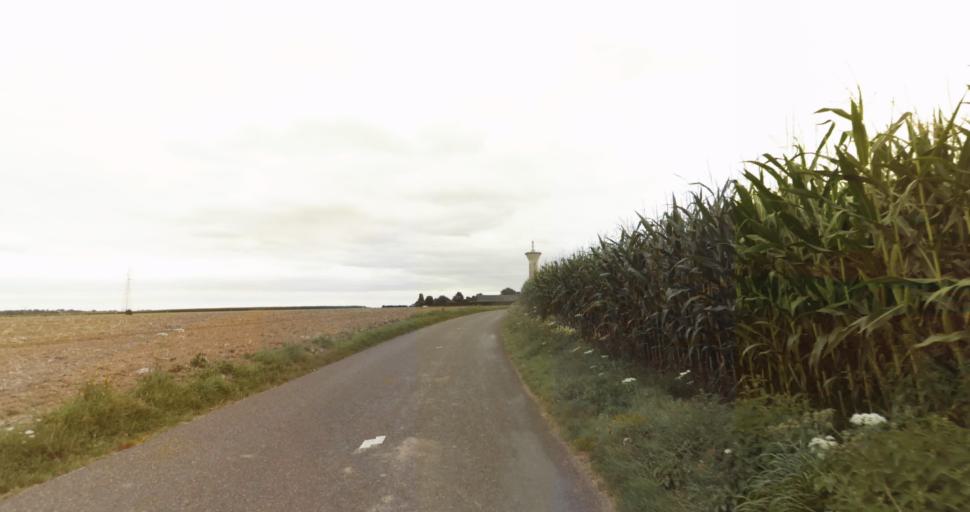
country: FR
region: Haute-Normandie
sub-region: Departement de l'Eure
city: Menilles
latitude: 48.9646
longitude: 1.2887
